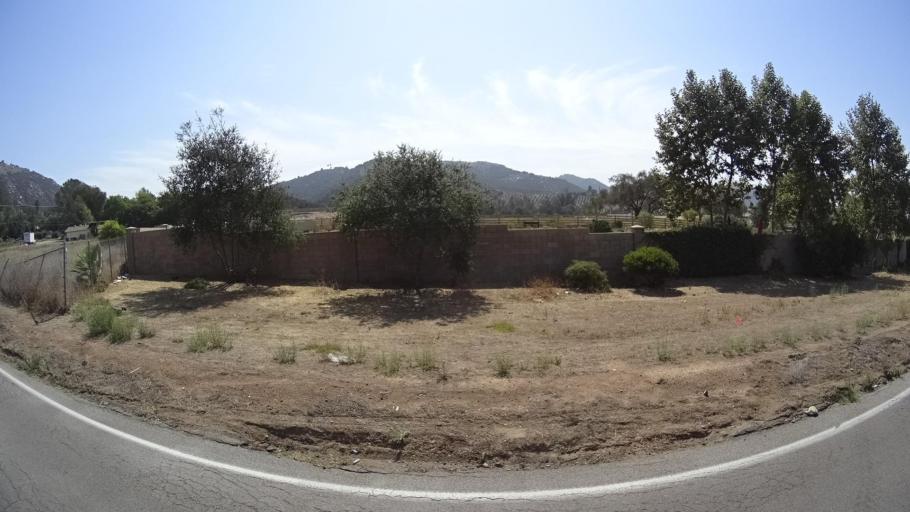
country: US
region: California
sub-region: San Diego County
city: Hidden Meadows
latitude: 33.1938
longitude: -117.1517
